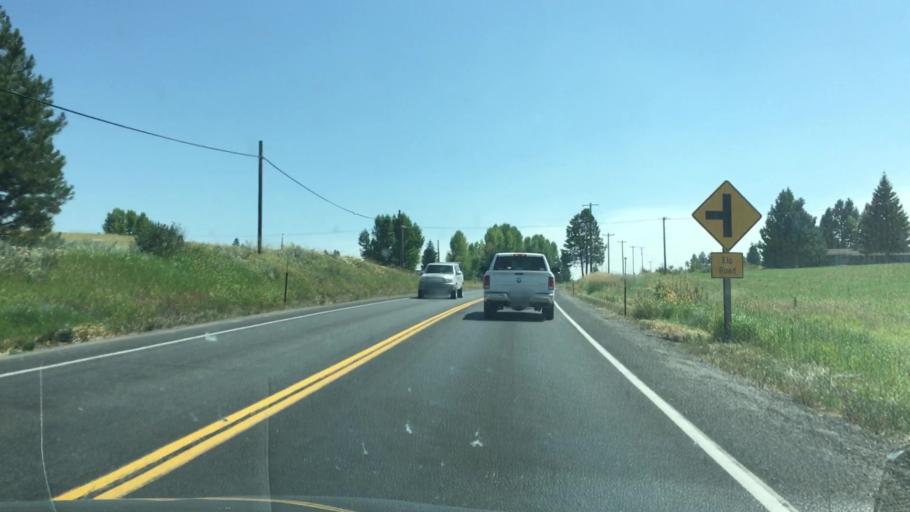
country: US
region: Idaho
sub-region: Valley County
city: McCall
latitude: 44.8848
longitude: -116.0911
